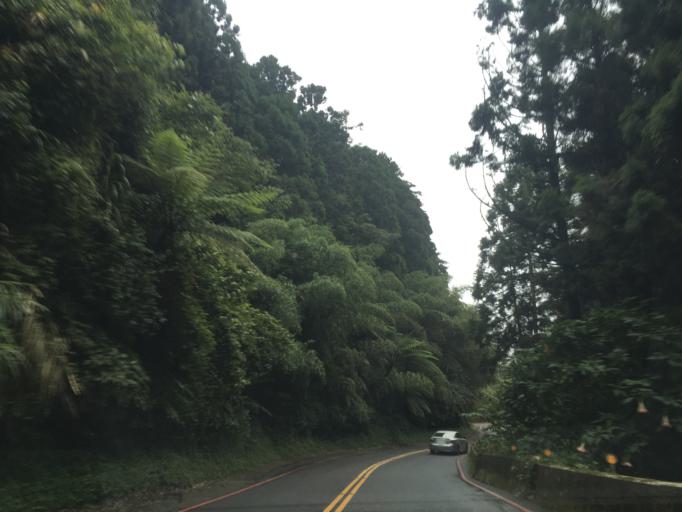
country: TW
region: Taiwan
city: Lugu
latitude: 23.5037
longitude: 120.6983
